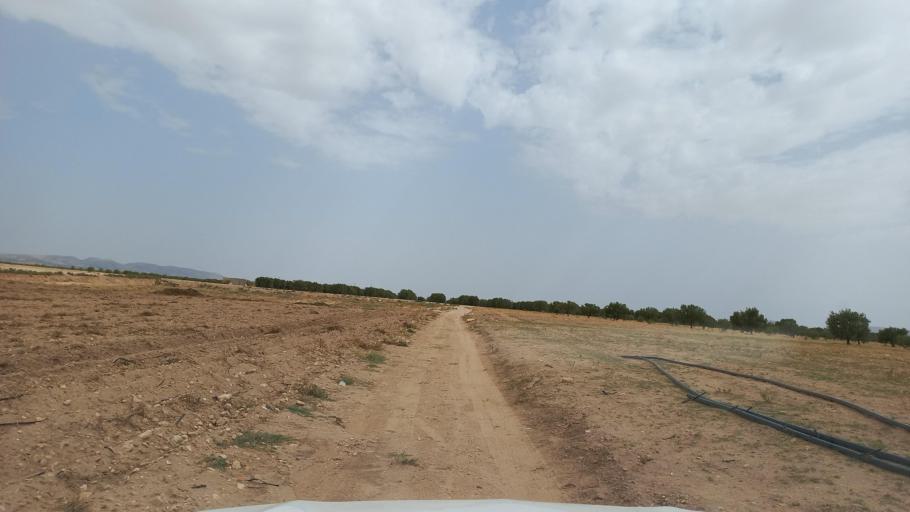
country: TN
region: Al Qasrayn
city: Kasserine
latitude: 35.2784
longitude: 9.0124
